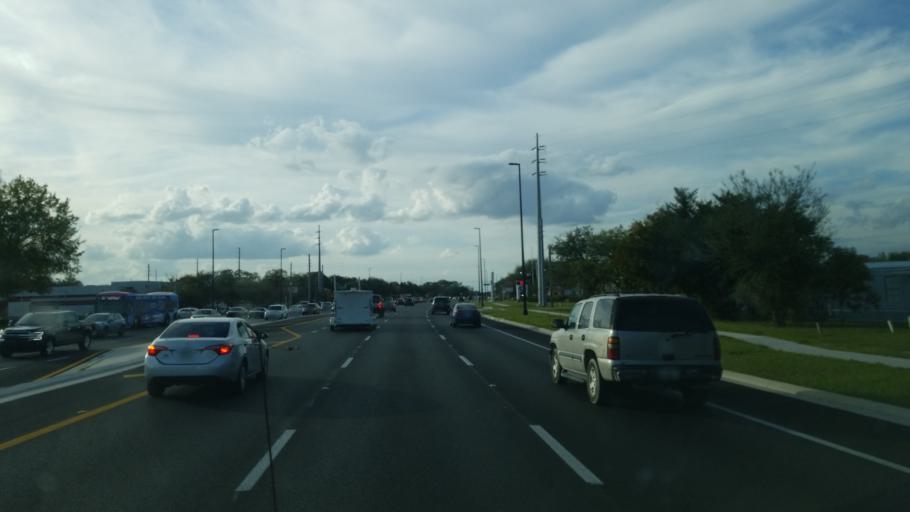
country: US
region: Florida
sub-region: Osceola County
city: Saint Cloud
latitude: 28.2479
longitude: -81.3076
